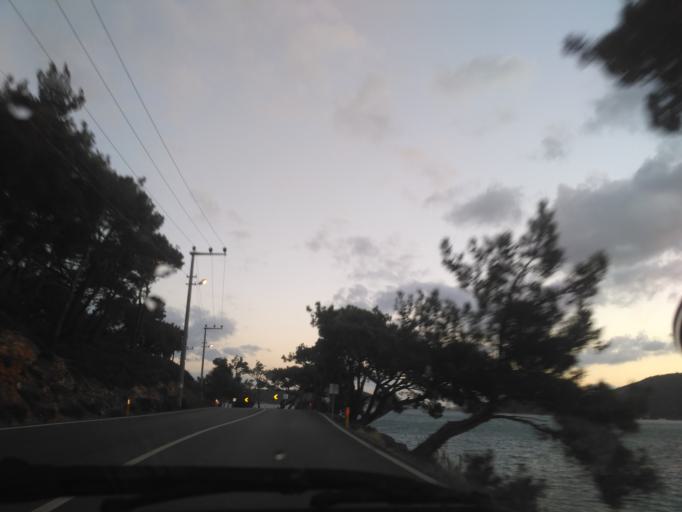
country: TR
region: Balikesir
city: Ayvalik
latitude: 39.2937
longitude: 26.6674
